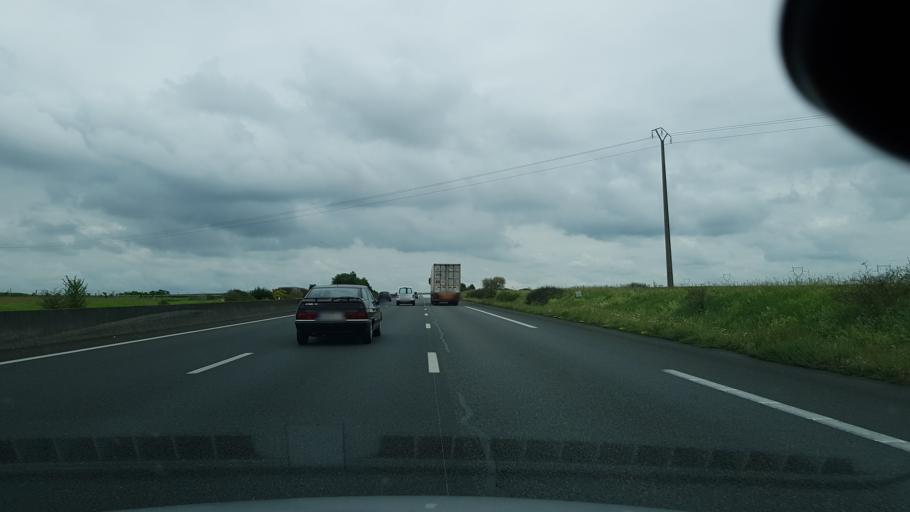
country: FR
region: Centre
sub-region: Departement du Loir-et-Cher
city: Suevres
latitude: 47.6994
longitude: 1.4442
